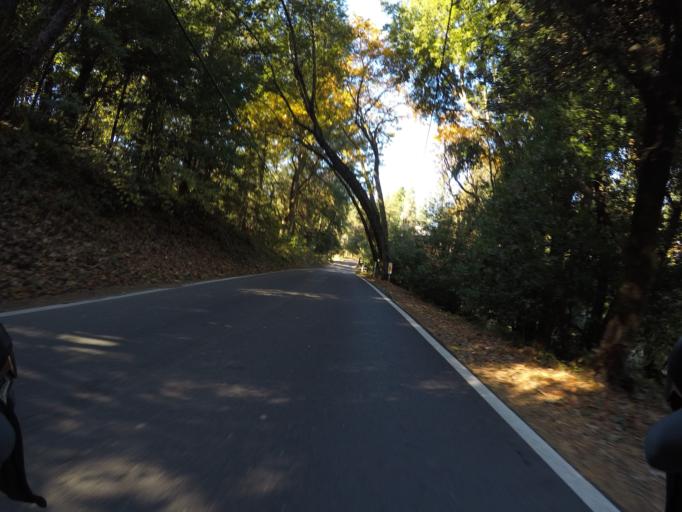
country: US
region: California
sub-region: Santa Clara County
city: Lexington Hills
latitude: 37.1519
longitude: -121.9964
